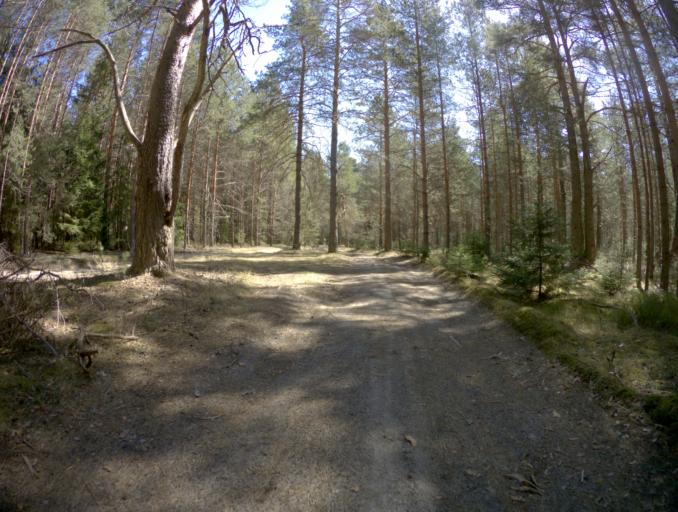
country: RU
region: Vladimir
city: Golovino
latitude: 55.9107
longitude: 40.4390
